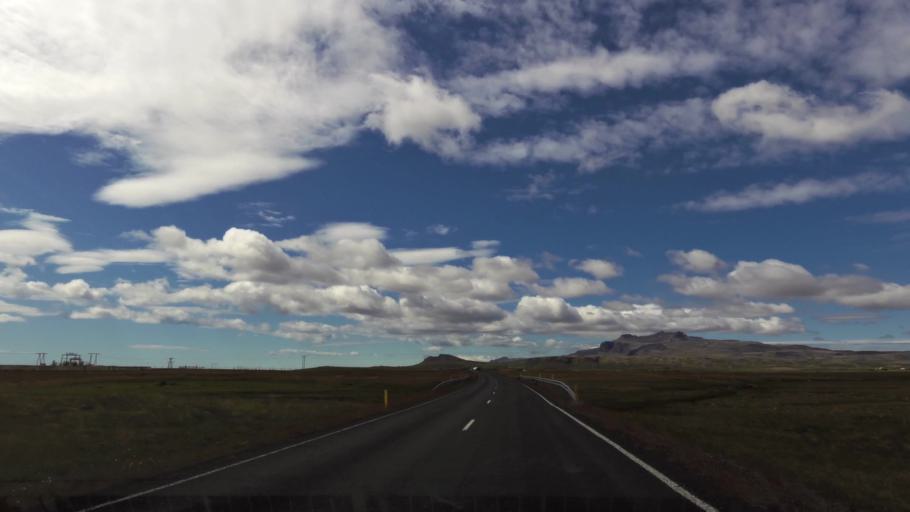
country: IS
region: West
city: Stykkisholmur
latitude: 64.8504
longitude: -22.7155
